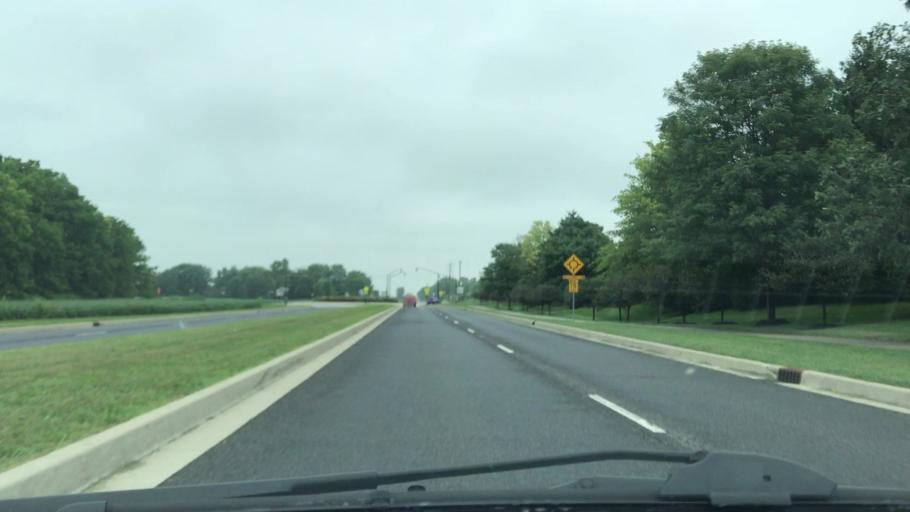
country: US
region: Indiana
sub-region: Hamilton County
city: Westfield
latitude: 40.0633
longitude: -86.0713
